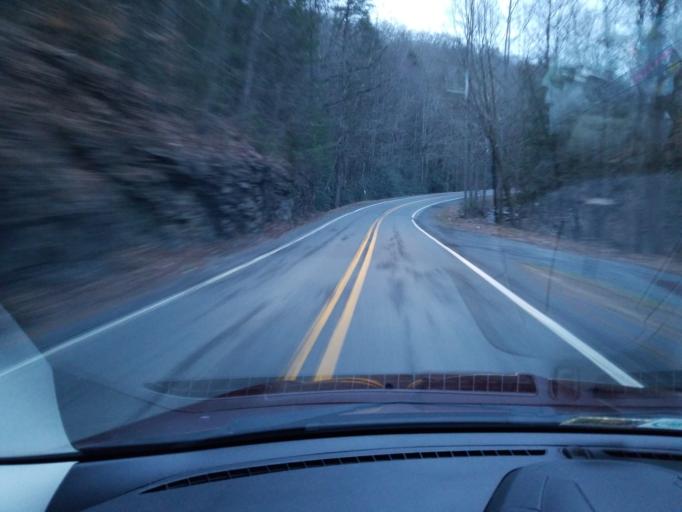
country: US
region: West Virginia
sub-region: Greenbrier County
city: Fairlea
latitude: 37.7594
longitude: -80.3975
